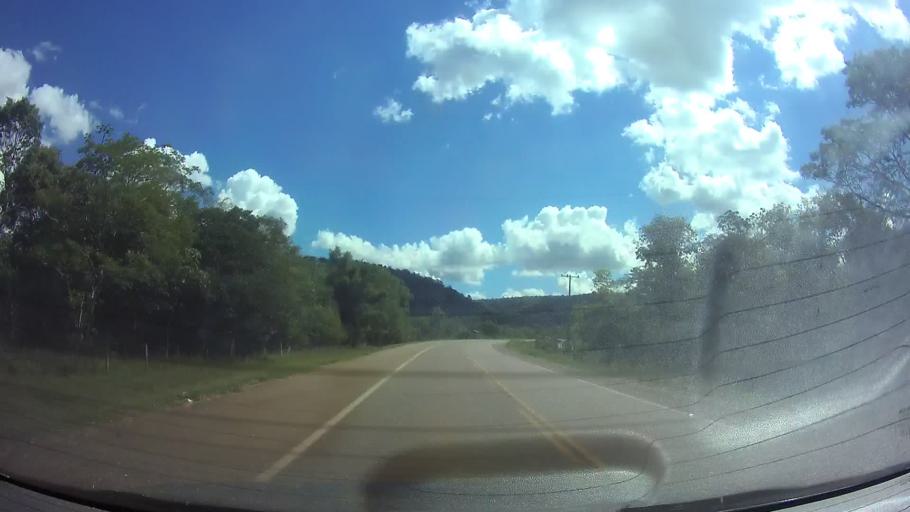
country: PY
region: Paraguari
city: La Colmena
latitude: -25.9173
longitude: -56.7190
